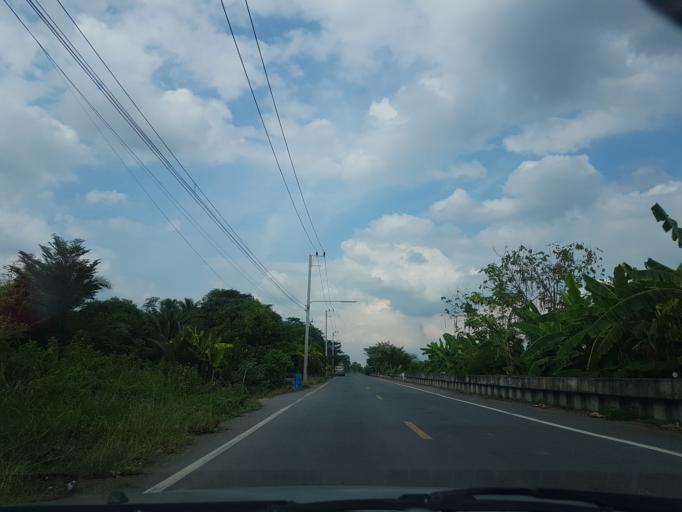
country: TH
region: Pathum Thani
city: Nong Suea
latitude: 14.1853
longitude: 100.8915
